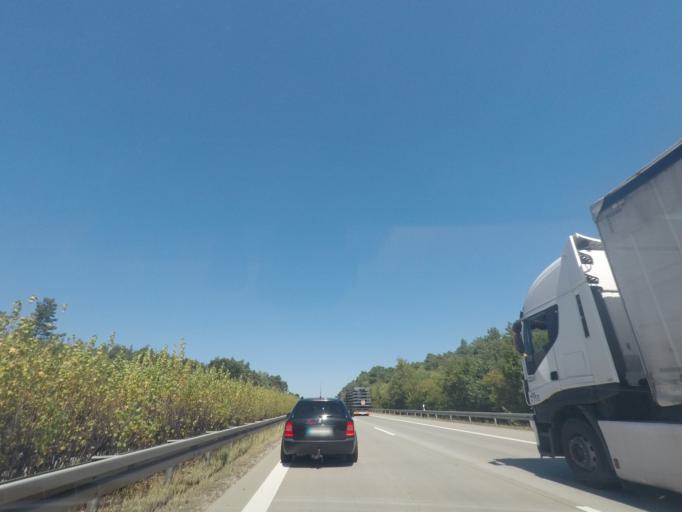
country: DE
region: Brandenburg
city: Bestensee
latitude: 52.2333
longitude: 13.5935
